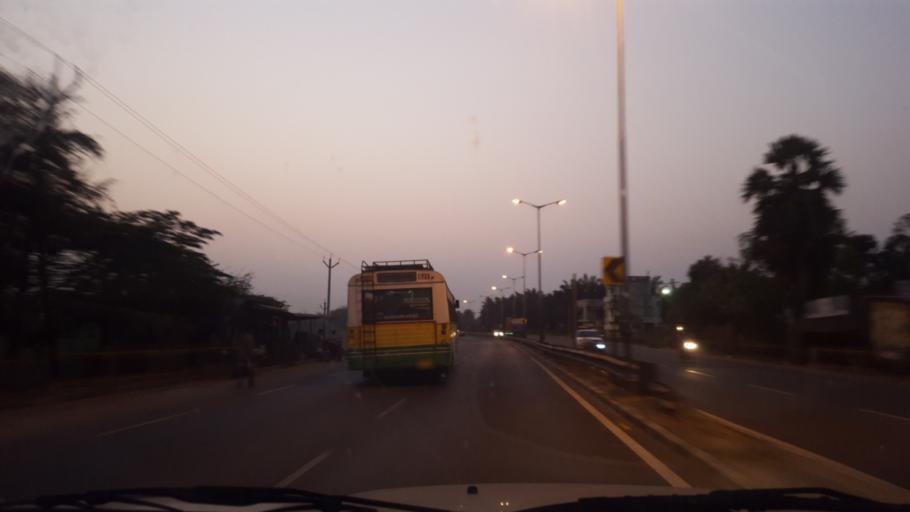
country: IN
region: Andhra Pradesh
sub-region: East Godavari
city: Peddapuram
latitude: 17.1579
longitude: 81.9955
